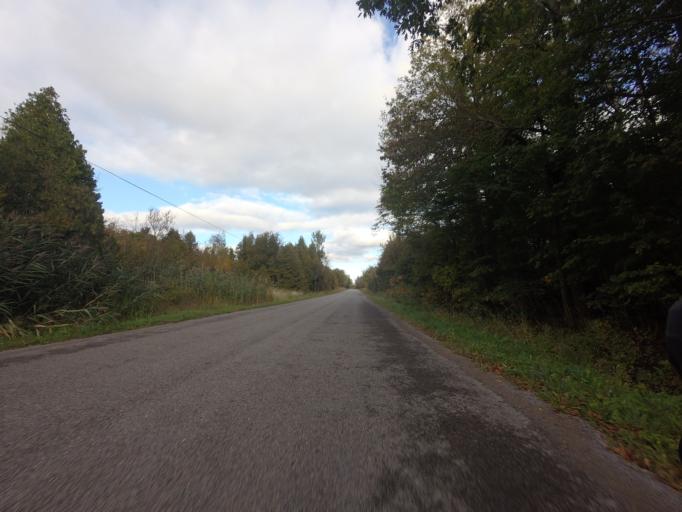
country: CA
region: Ontario
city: Cobourg
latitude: 43.9818
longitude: -77.9840
